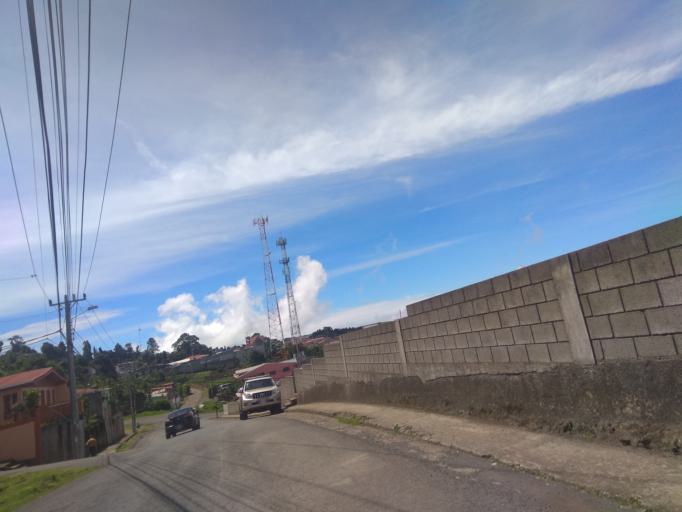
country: CR
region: Cartago
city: Cot
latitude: 9.9162
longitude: -83.8966
